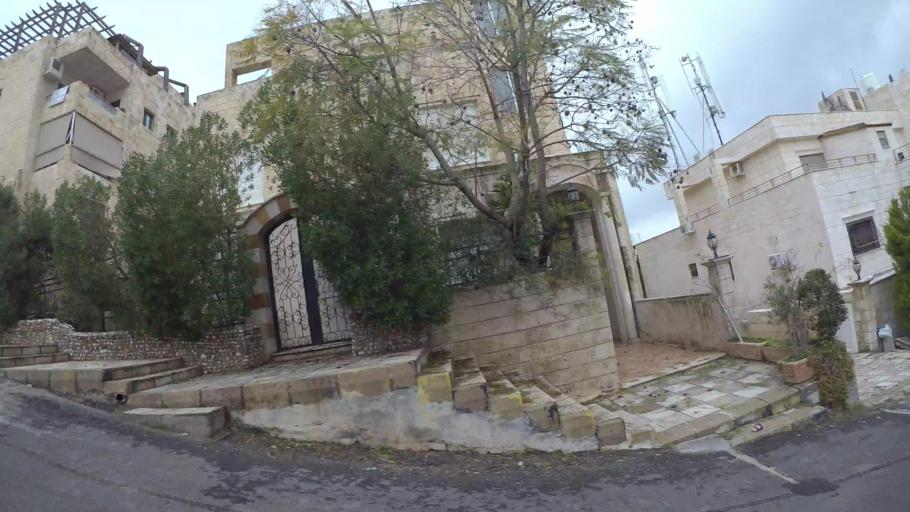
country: JO
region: Amman
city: Al Bunayyat ash Shamaliyah
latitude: 31.9412
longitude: 35.8945
